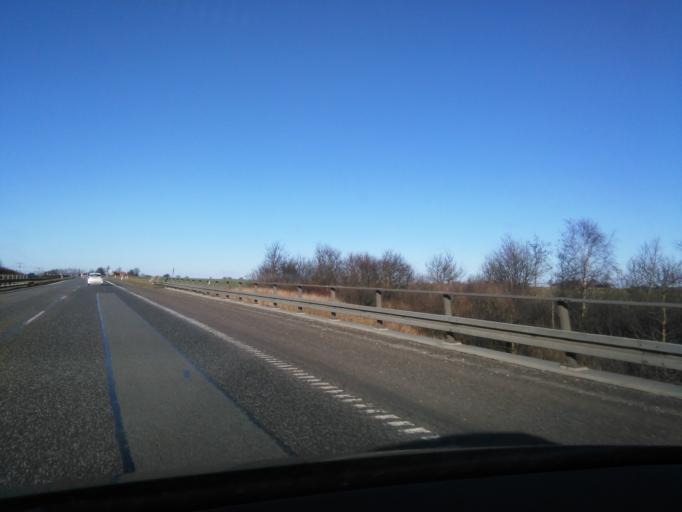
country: DK
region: Central Jutland
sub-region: Randers Kommune
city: Randers
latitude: 56.4911
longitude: 9.9803
